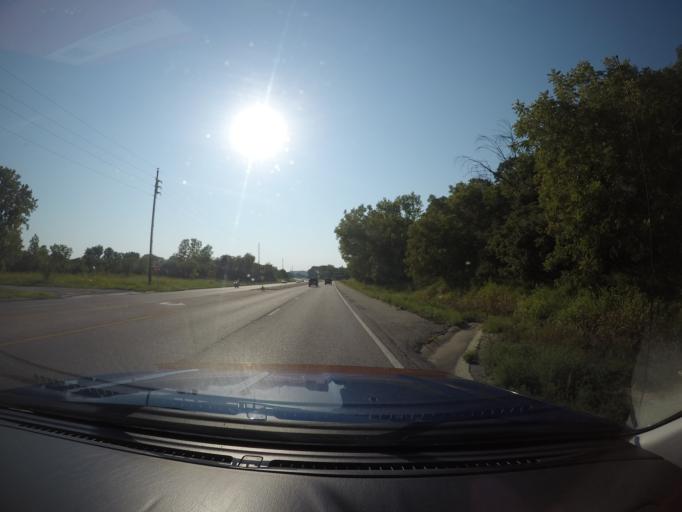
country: US
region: Kansas
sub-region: Wyandotte County
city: Edwardsville
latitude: 39.0633
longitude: -94.8288
